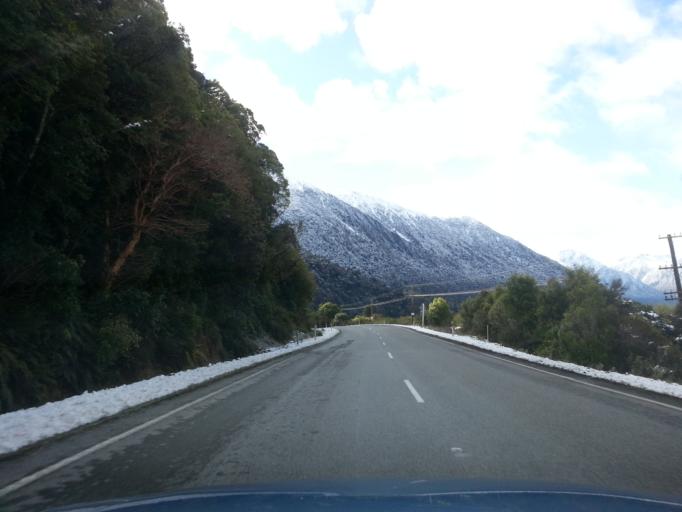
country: NZ
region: West Coast
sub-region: Grey District
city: Greymouth
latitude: -42.8160
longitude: 171.5650
